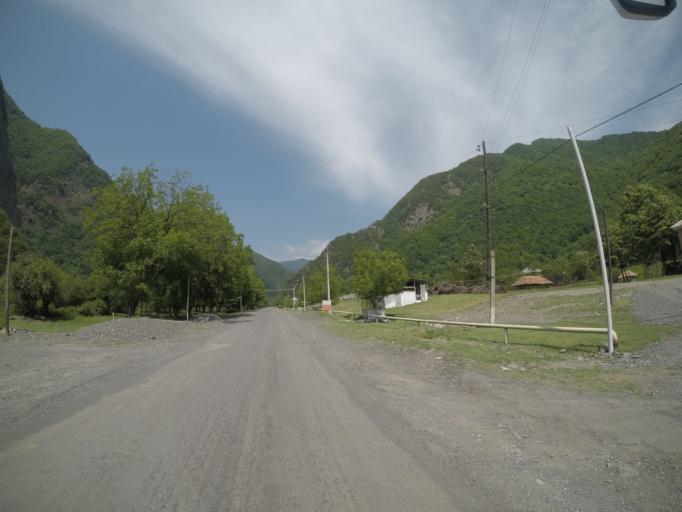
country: AZ
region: Qakh Rayon
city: Qaxbas
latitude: 41.4584
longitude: 47.0256
